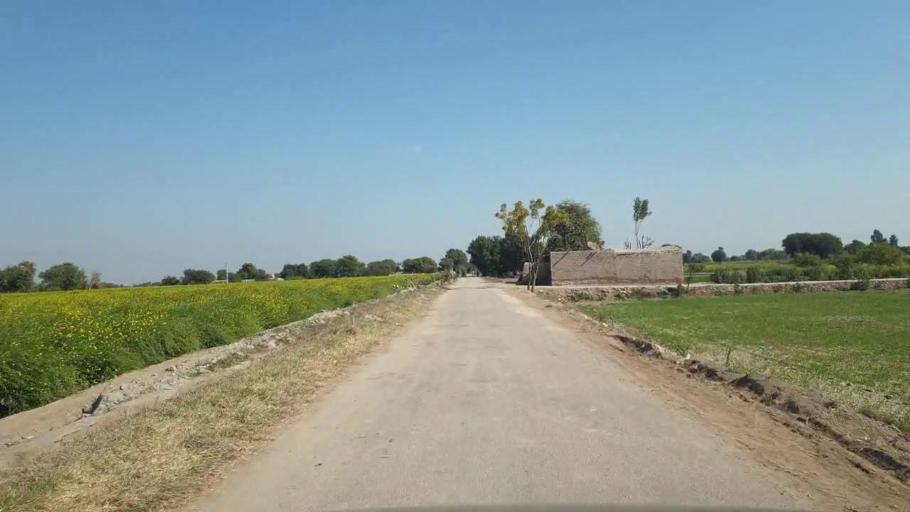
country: PK
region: Sindh
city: Shahpur Chakar
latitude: 26.1080
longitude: 68.6523
